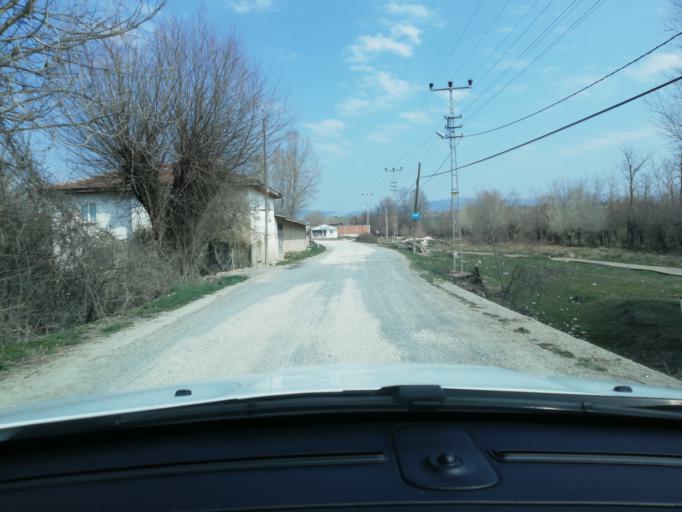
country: TR
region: Kastamonu
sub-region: Cide
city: Kastamonu
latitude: 41.4547
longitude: 33.7673
